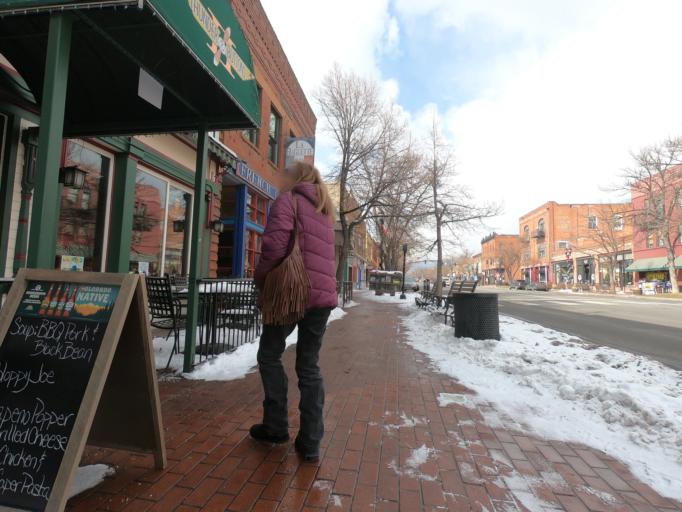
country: US
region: Colorado
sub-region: El Paso County
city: Colorado Springs
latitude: 38.8466
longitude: -104.8620
